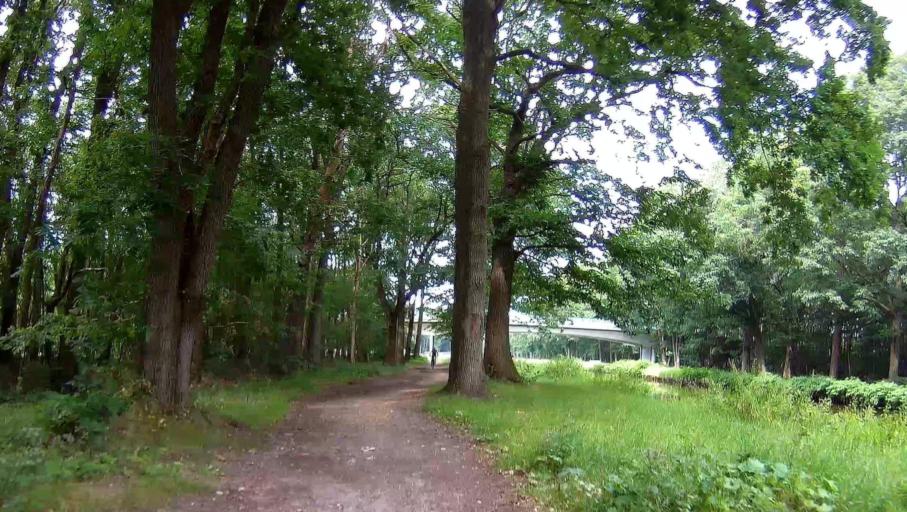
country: BE
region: Flanders
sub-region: Provincie Antwerpen
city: Dessel
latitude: 51.2400
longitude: 5.1625
